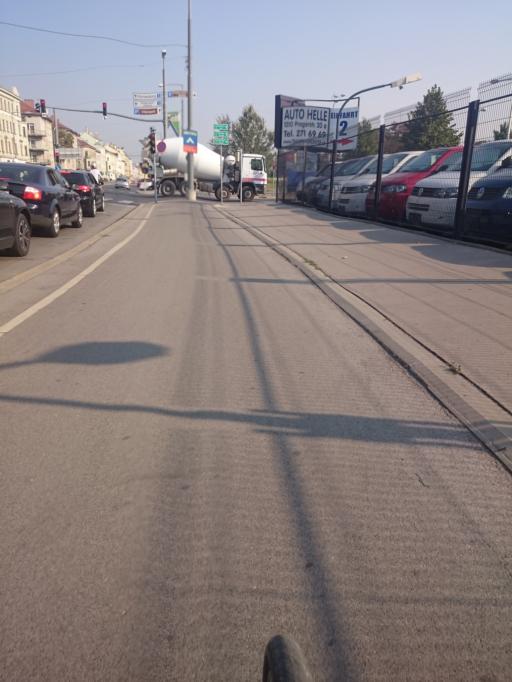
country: AT
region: Lower Austria
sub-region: Politischer Bezirk Korneuburg
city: Langenzersdorf
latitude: 48.2635
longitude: 16.3945
